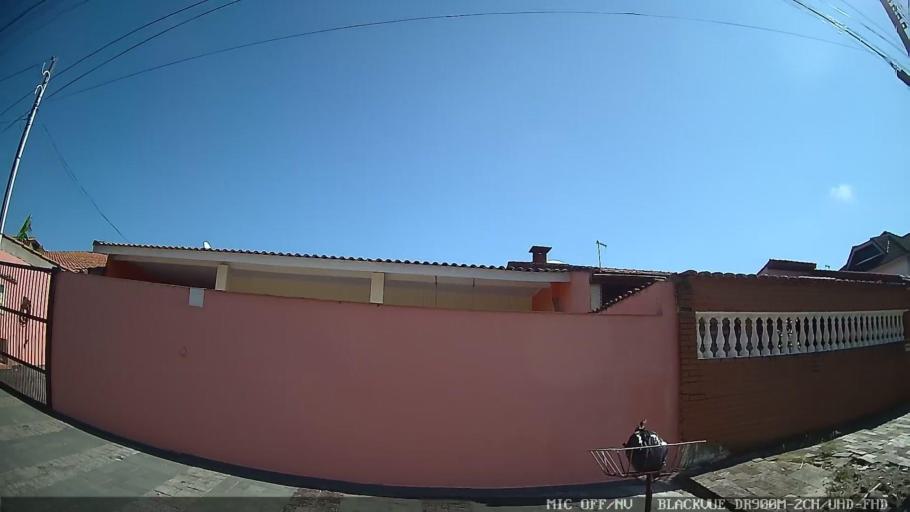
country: BR
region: Sao Paulo
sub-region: Peruibe
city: Peruibe
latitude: -24.2922
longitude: -46.9701
